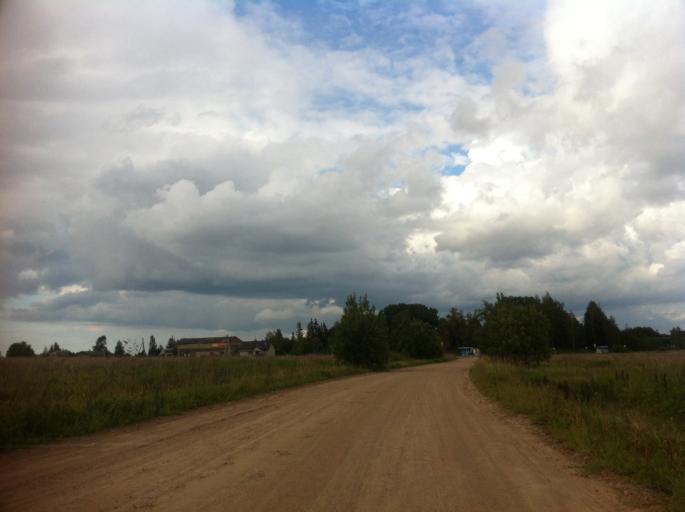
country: RU
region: Pskov
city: Izborsk
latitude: 57.8357
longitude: 27.9862
